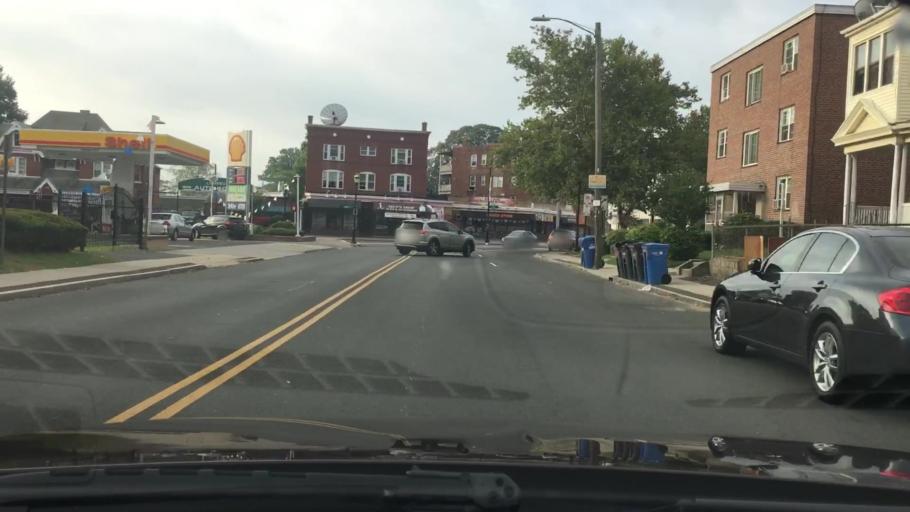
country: US
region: Connecticut
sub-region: Hartford County
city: Hartford
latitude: 41.7579
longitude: -72.7062
